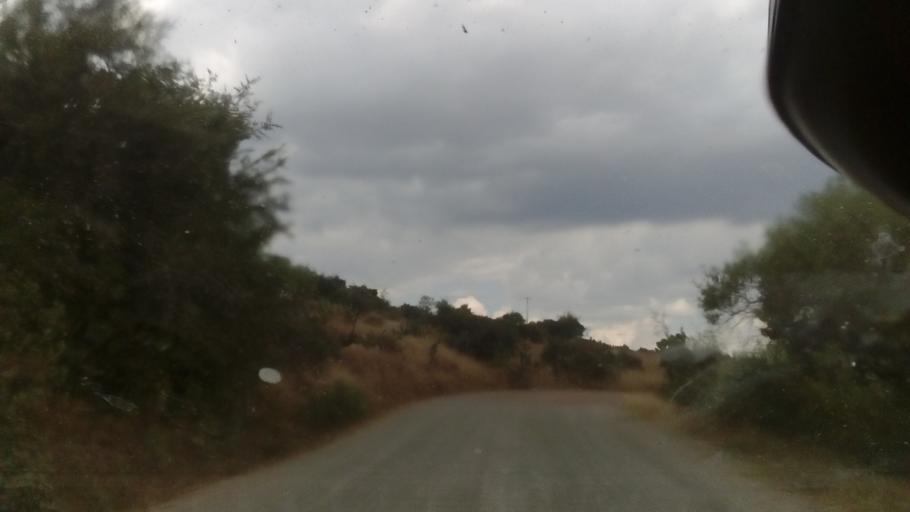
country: MX
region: Guanajuato
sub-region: Silao de la Victoria
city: San Francisco (Banos de Agua Caliente)
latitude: 21.2001
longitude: -101.4520
